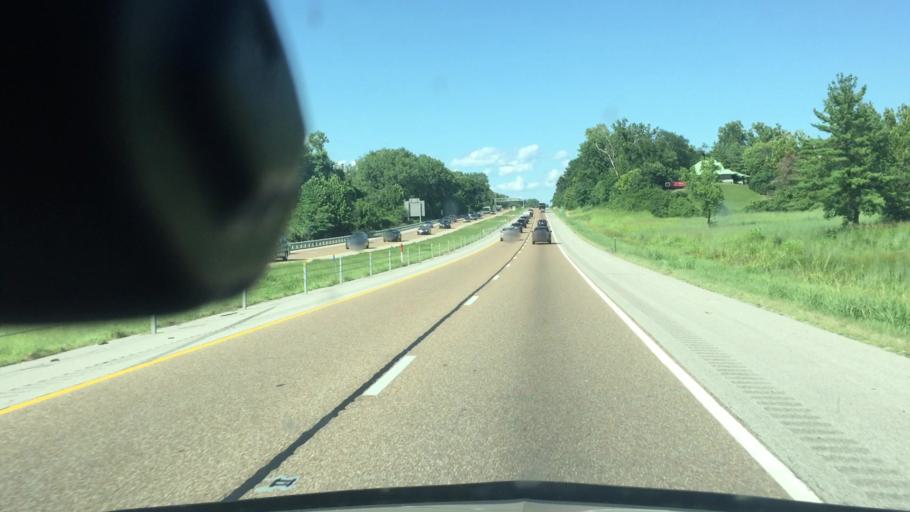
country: US
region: Illinois
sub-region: Madison County
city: Collinsville
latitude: 38.6896
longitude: -90.0016
